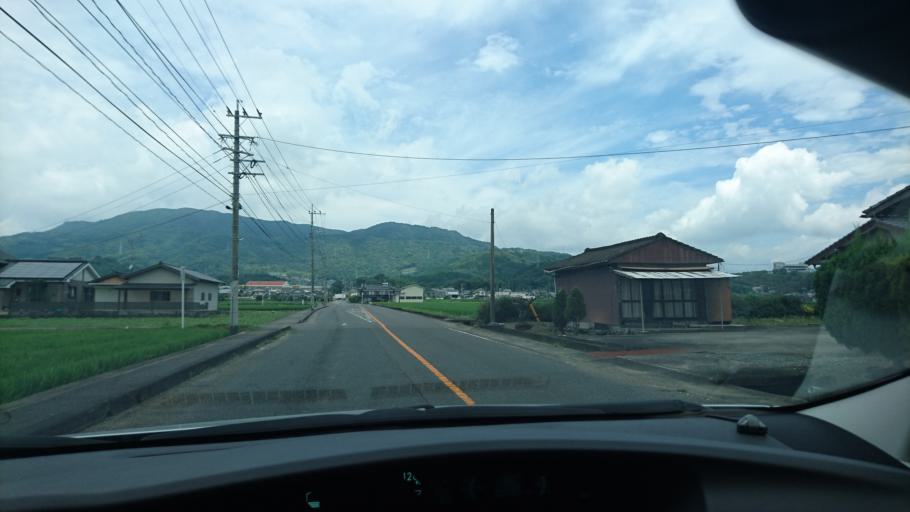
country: JP
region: Saga Prefecture
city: Takeocho-takeo
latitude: 33.2090
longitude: 130.1215
